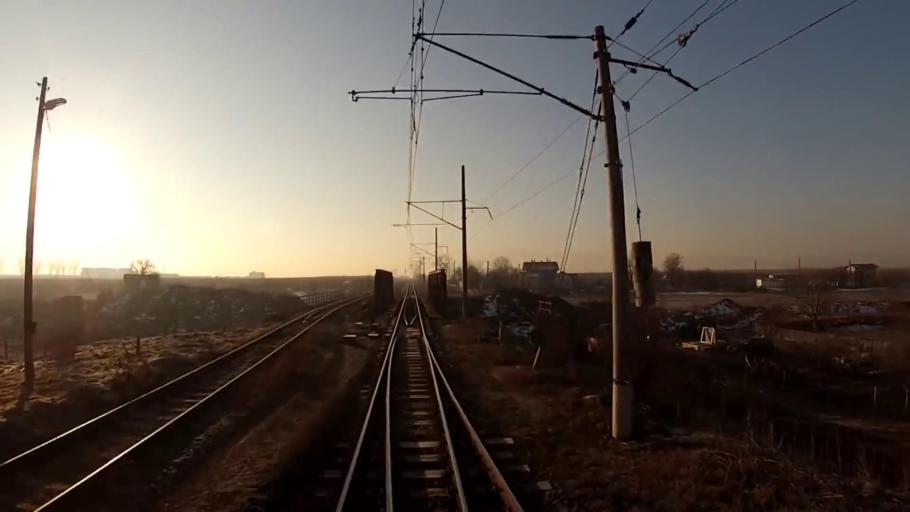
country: BG
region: Sofiya
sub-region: Obshtina Kostinbrod
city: Kostinbrod
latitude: 42.7973
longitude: 23.2065
